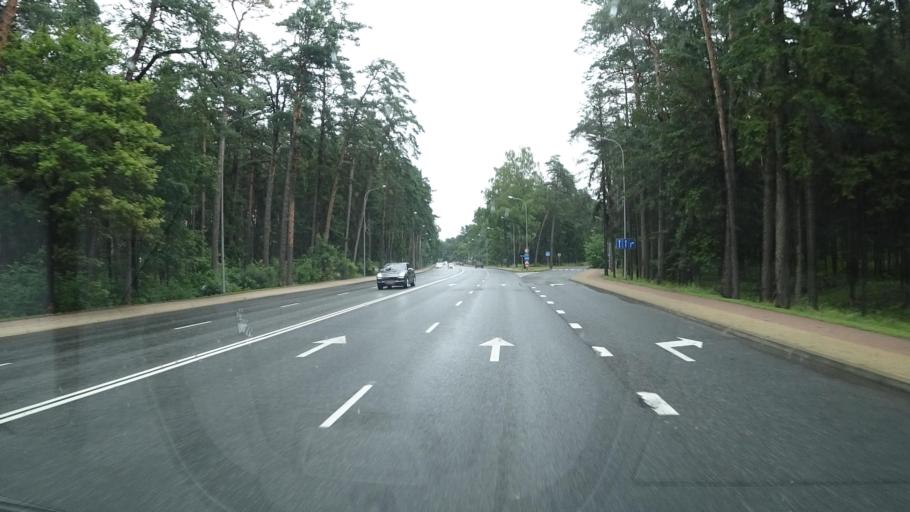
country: LV
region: Jurmala
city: Jurmala
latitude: 56.9741
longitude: 23.8432
